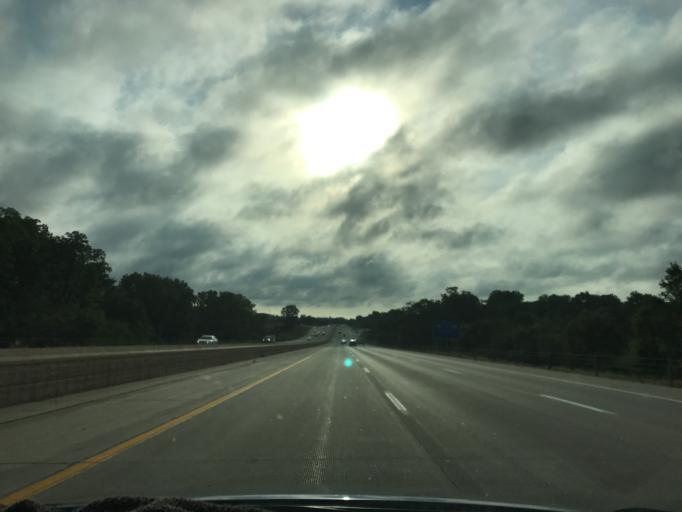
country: US
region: Iowa
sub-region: Johnson County
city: Iowa City
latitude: 41.6869
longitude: -91.5112
